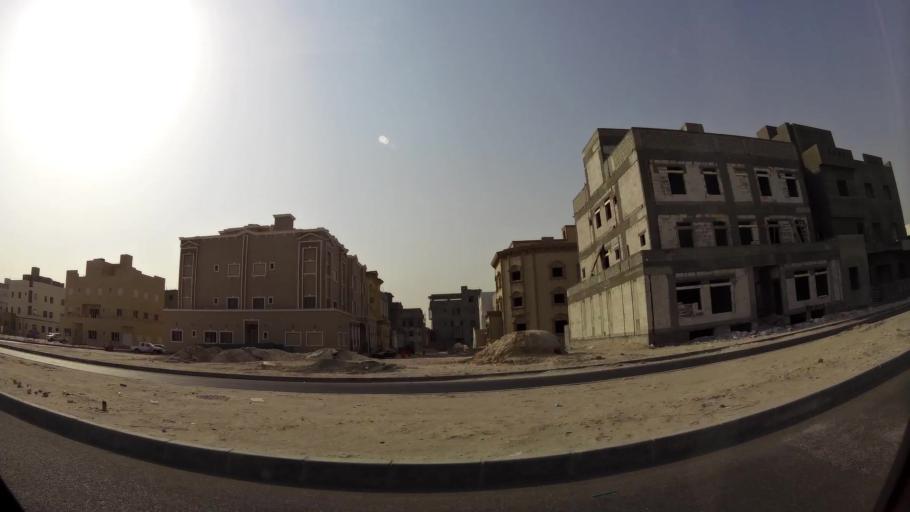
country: KW
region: Al Asimah
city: Ar Rabiyah
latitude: 29.3279
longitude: 47.8081
